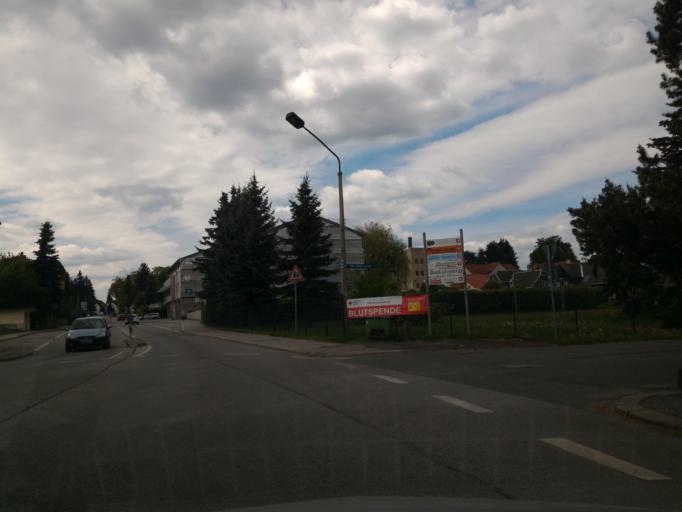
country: DE
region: Saxony
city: Neugersdorf
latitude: 50.9856
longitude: 14.6133
